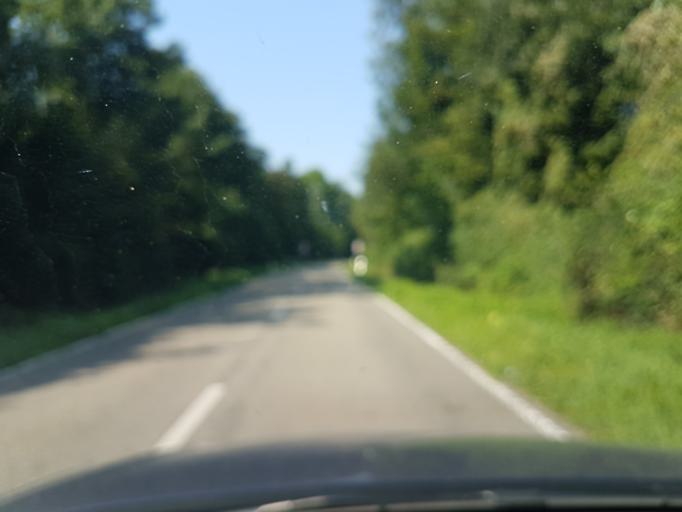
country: DE
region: Rheinland-Pfalz
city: Otterstadt
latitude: 49.3706
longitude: 8.4701
